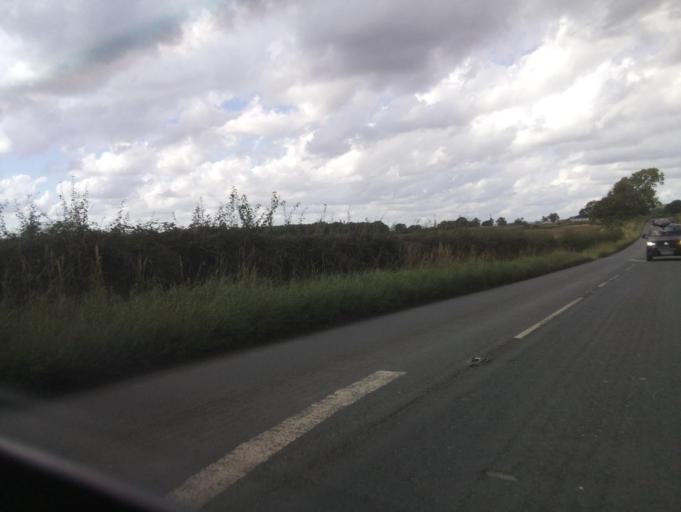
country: GB
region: England
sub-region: North Yorkshire
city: Bedale
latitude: 54.2160
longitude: -1.6303
